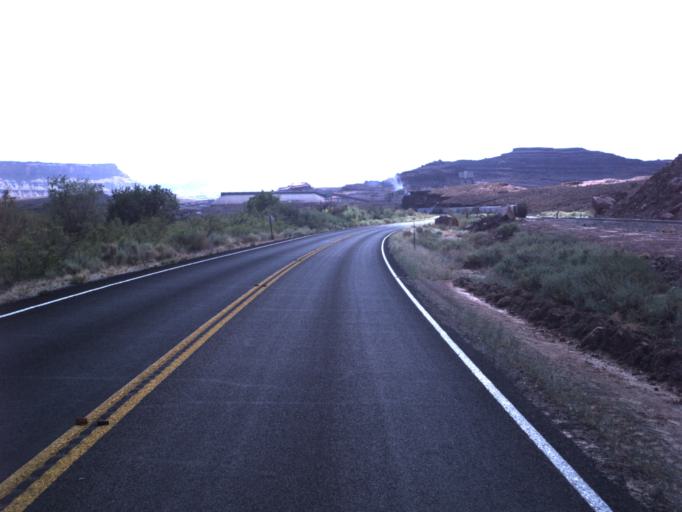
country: US
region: Utah
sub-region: Grand County
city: Moab
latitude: 38.5369
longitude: -109.6553
